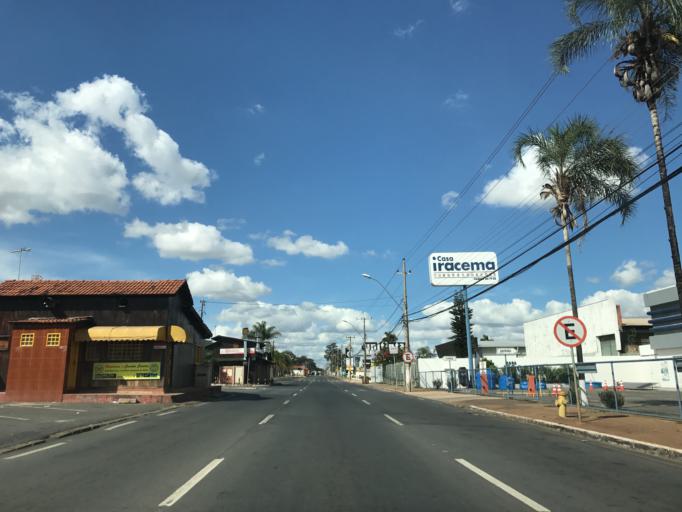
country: BR
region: Federal District
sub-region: Brasilia
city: Brasilia
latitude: -15.8039
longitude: -47.9605
